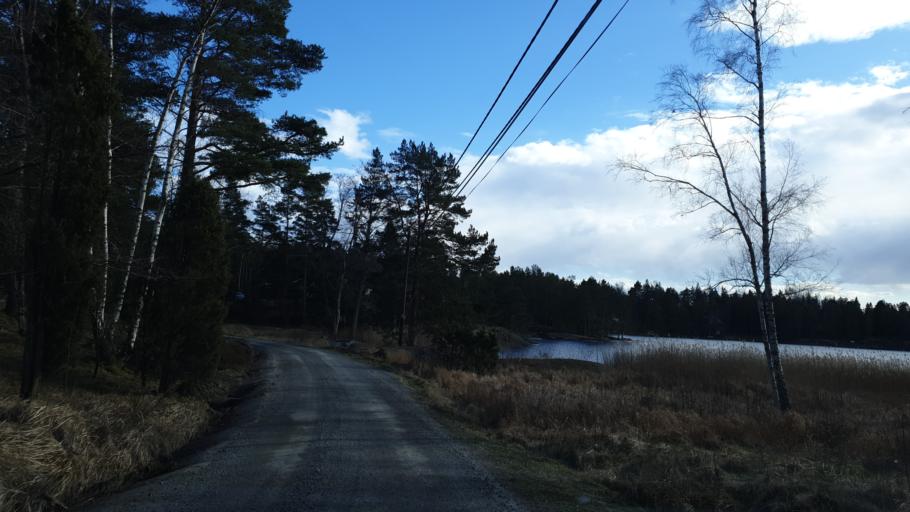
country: SE
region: Stockholm
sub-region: Varmdo Kommun
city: Holo
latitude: 59.2742
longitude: 18.6359
